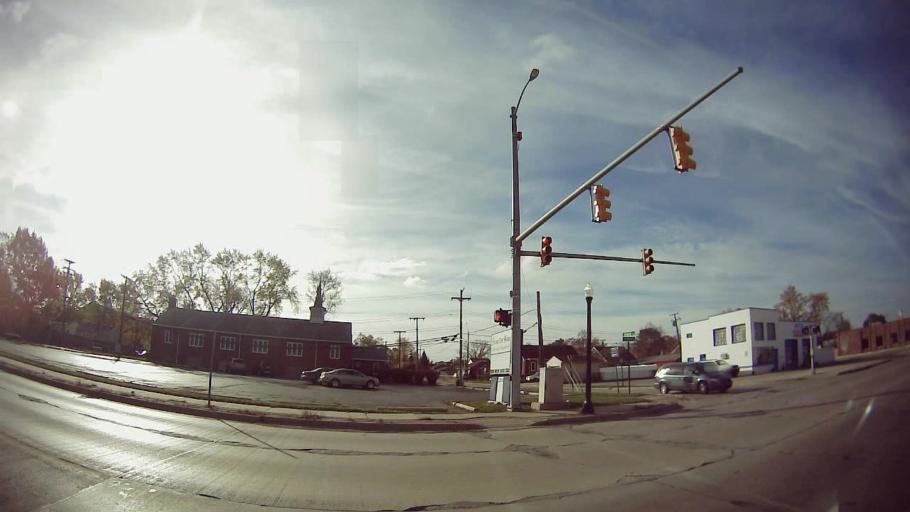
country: US
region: Michigan
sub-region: Oakland County
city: Hazel Park
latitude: 42.4615
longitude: -83.1009
